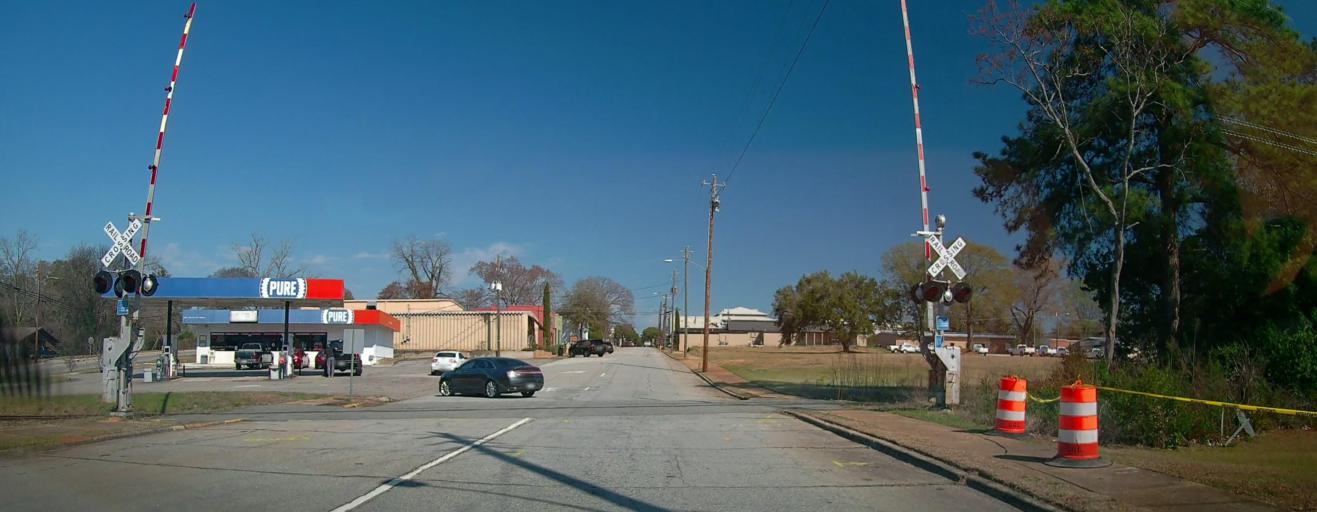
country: US
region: Georgia
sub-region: Houston County
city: Perry
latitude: 32.4571
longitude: -83.7371
